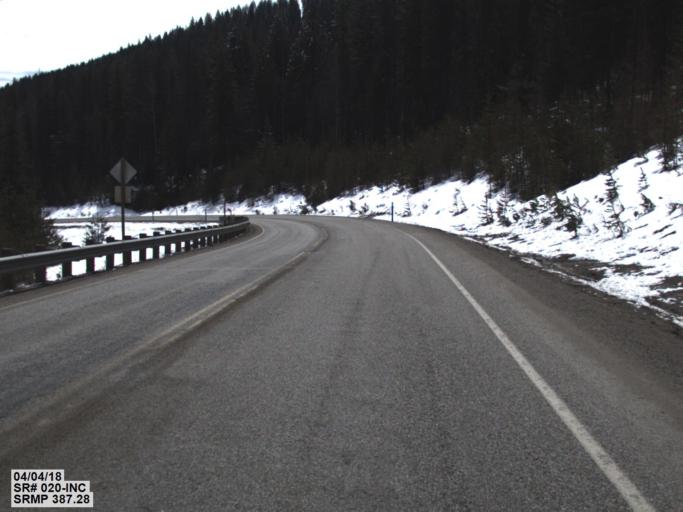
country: CA
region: British Columbia
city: Fruitvale
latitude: 48.6829
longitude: -117.4504
